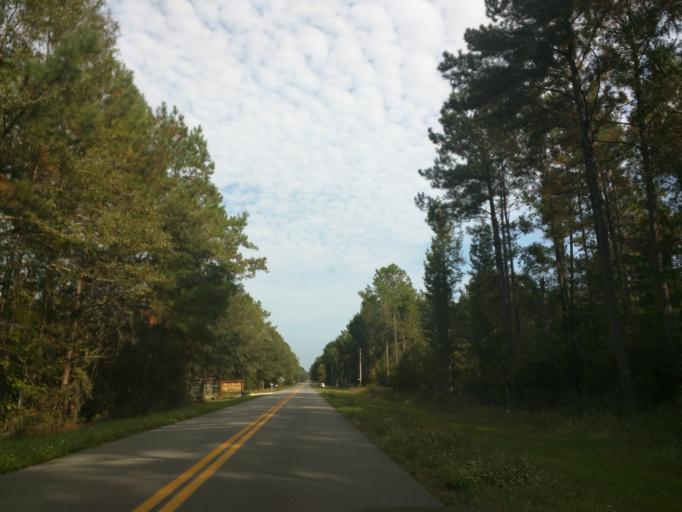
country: US
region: Florida
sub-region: Jefferson County
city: Monticello
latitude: 30.3433
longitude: -83.9908
